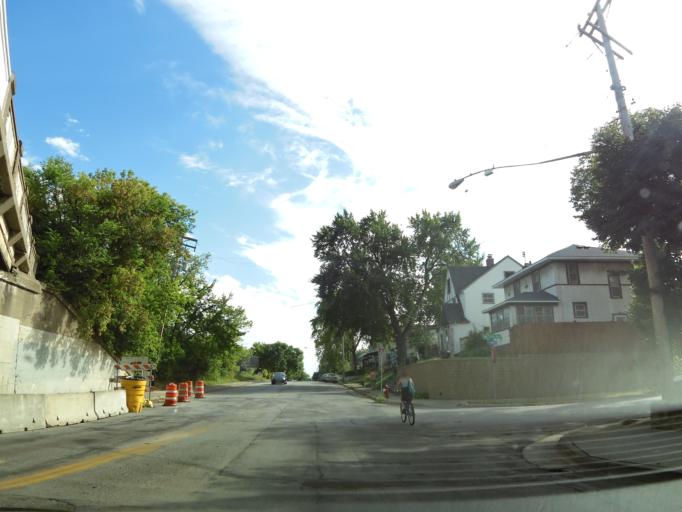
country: US
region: Minnesota
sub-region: Hennepin County
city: Minneapolis
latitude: 45.0054
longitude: -93.2525
